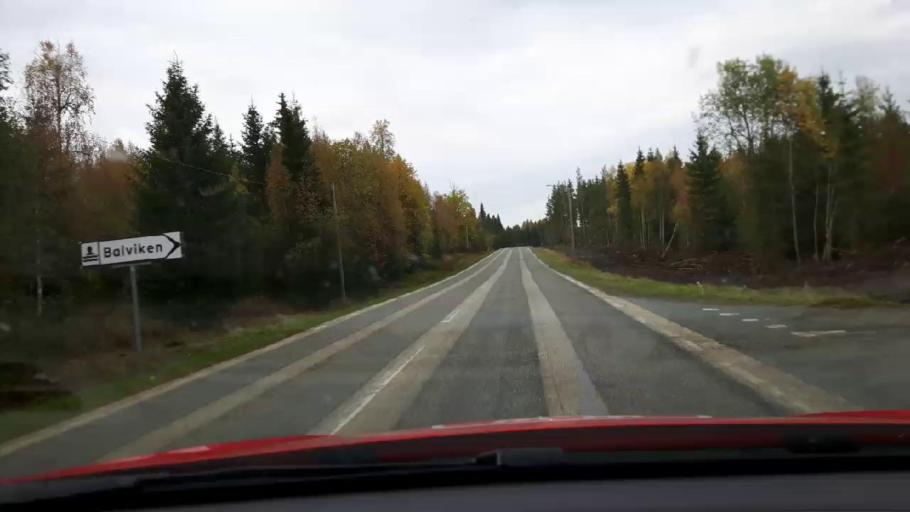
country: SE
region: Jaemtland
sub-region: Bergs Kommun
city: Hoverberg
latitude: 62.8190
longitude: 14.3980
